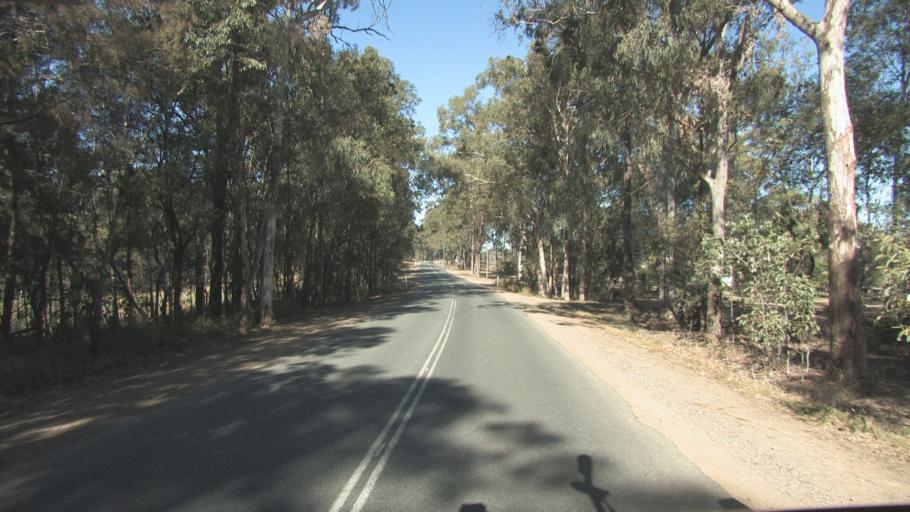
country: AU
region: Queensland
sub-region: Logan
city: North Maclean
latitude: -27.7478
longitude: 152.9914
